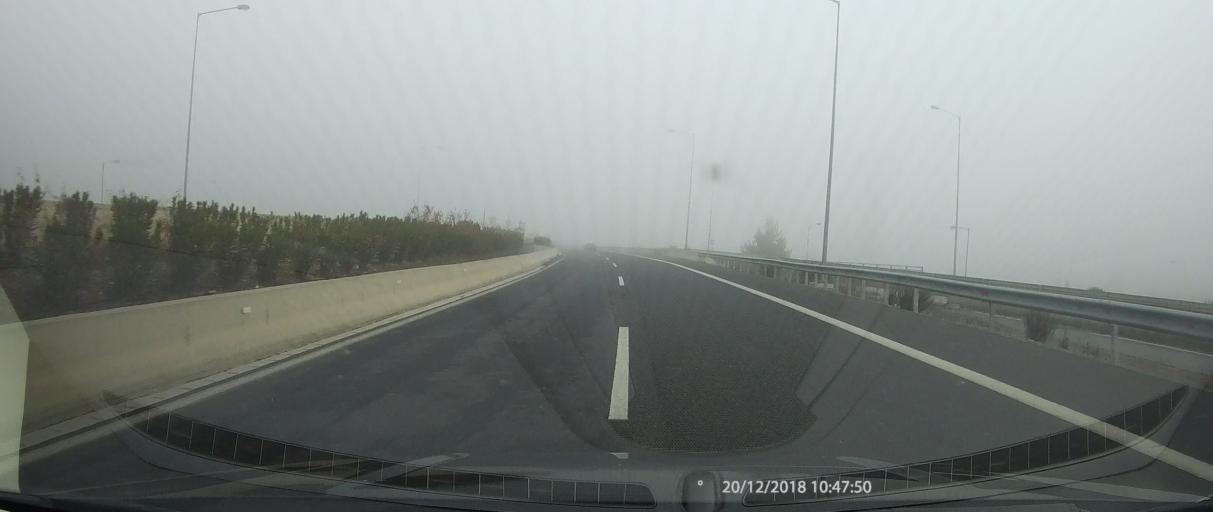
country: GR
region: Peloponnese
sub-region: Nomos Arkadias
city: Tripoli
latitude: 37.5037
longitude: 22.4001
